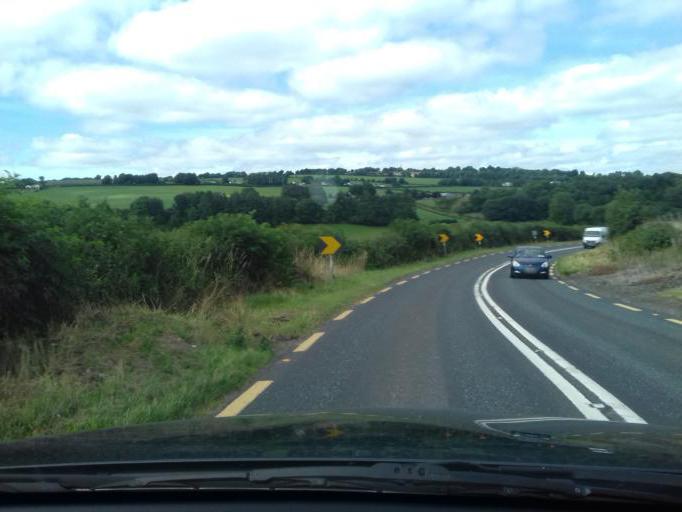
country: IE
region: Leinster
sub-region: Wicklow
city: Baltinglass
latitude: 52.9772
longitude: -6.6843
